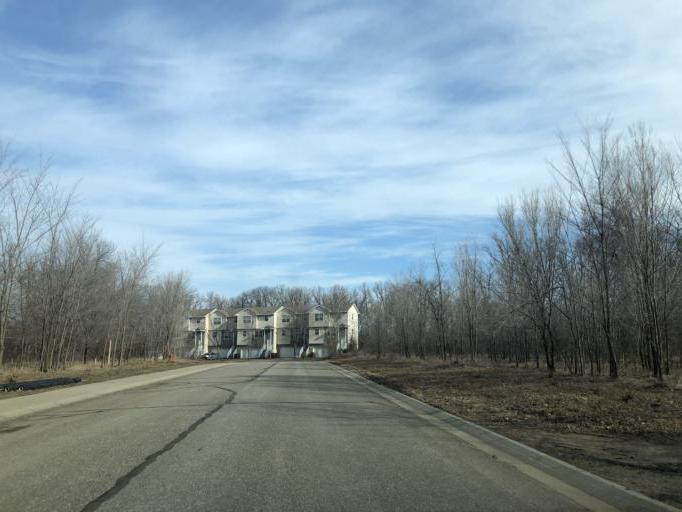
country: US
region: Minnesota
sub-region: Sherburne County
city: Becker
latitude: 45.3997
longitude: -93.8523
